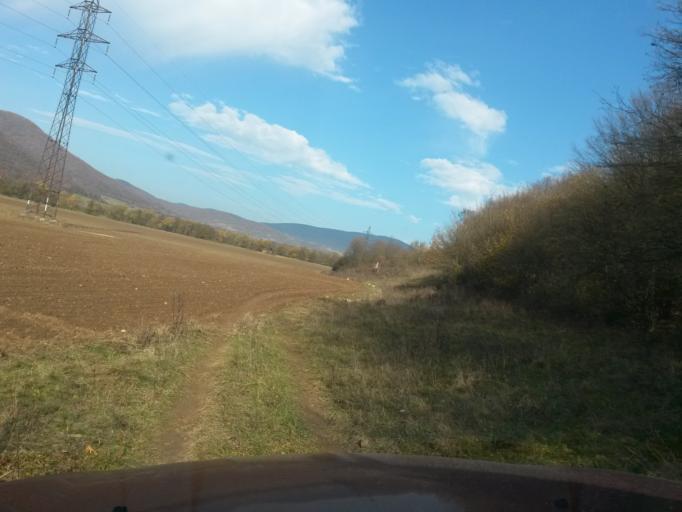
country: SK
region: Kosicky
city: Roznava
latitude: 48.5987
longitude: 20.4844
